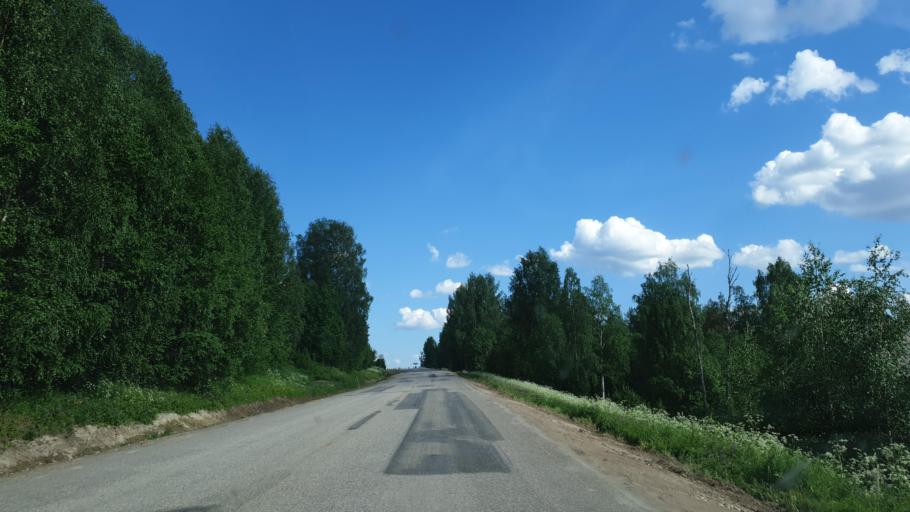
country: SE
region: Norrbotten
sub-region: Alvsbyns Kommun
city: AElvsbyn
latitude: 65.8554
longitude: 20.4310
